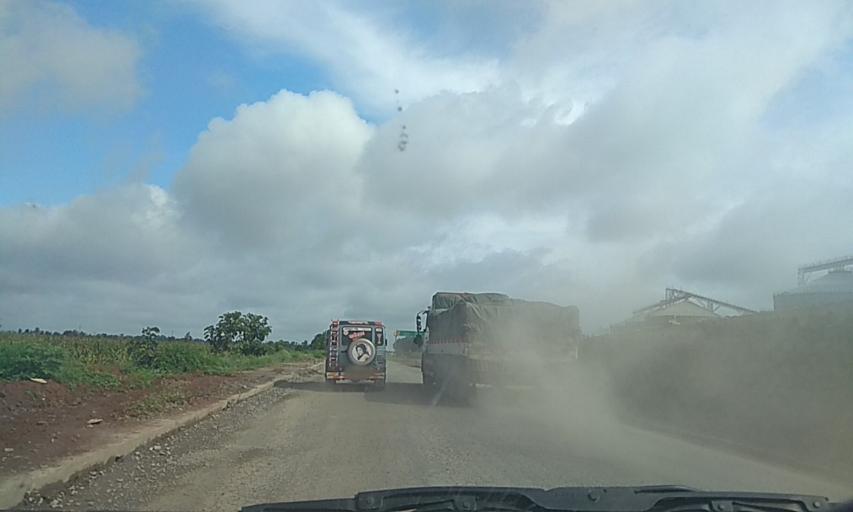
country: IN
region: Karnataka
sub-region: Haveri
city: Shiggaon
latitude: 15.0419
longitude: 75.1714
